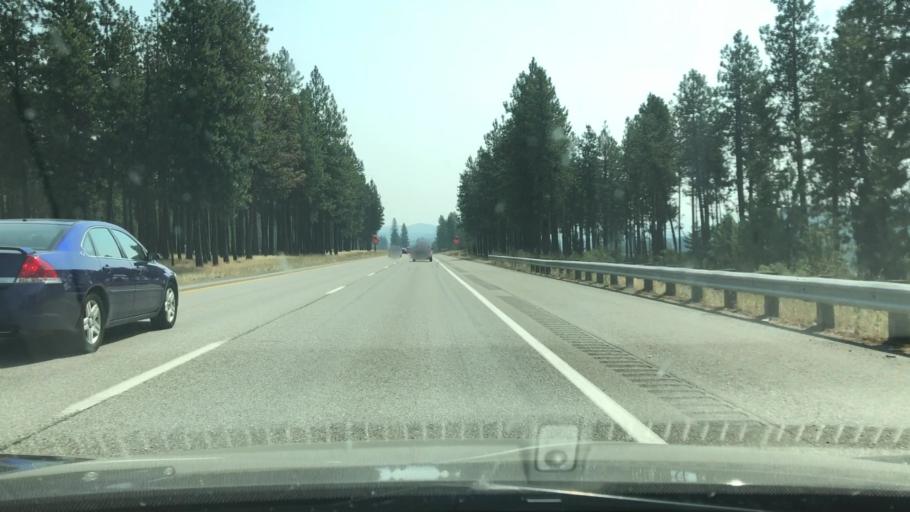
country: US
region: Idaho
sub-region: Kootenai County
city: Coeur d'Alene
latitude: 47.7063
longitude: -116.8460
